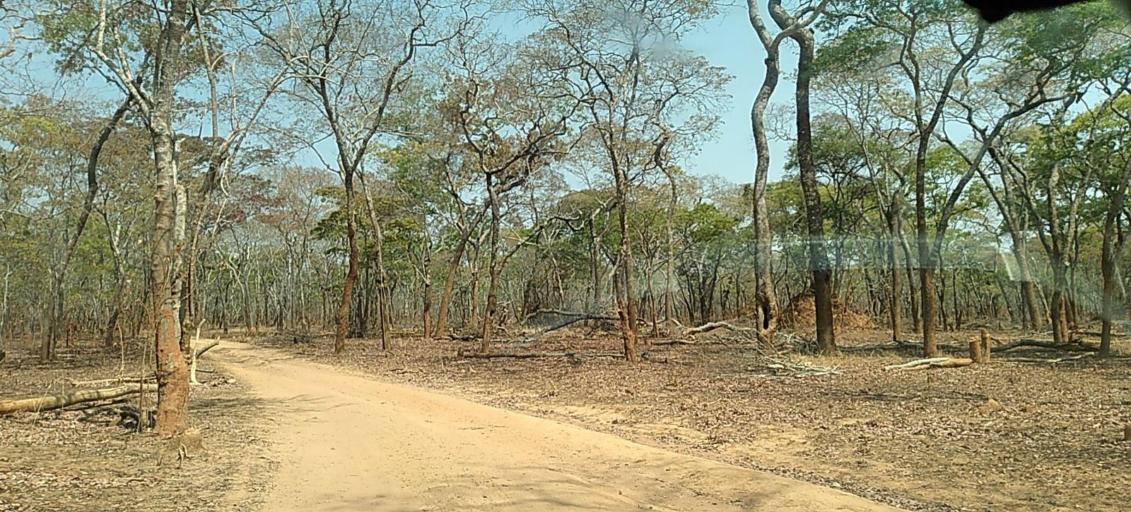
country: ZM
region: North-Western
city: Kasempa
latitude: -13.3927
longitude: 25.6059
